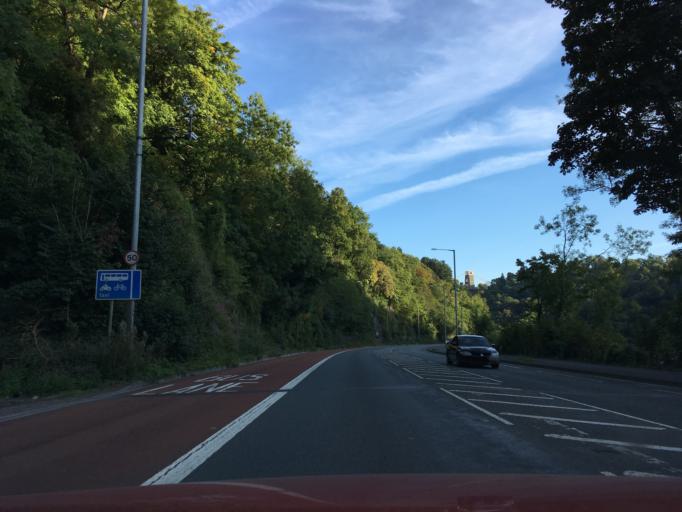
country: GB
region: England
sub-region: Bristol
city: Bristol
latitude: 51.4619
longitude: -2.6301
